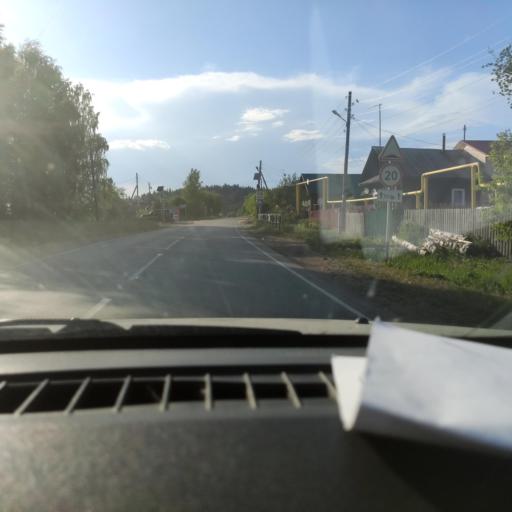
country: RU
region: Perm
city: Krasnokamsk
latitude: 58.1436
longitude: 55.7310
